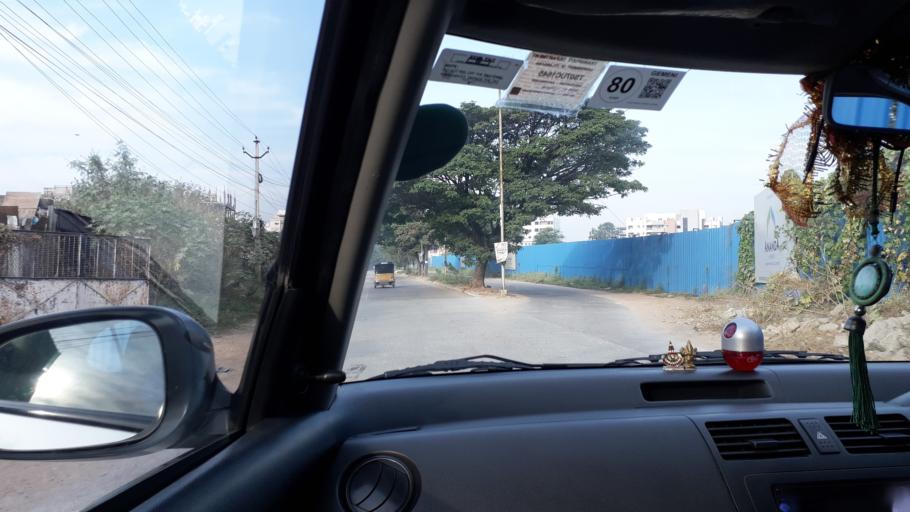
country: IN
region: Telangana
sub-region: Hyderabad
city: Hyderabad
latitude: 17.3939
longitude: 78.3803
